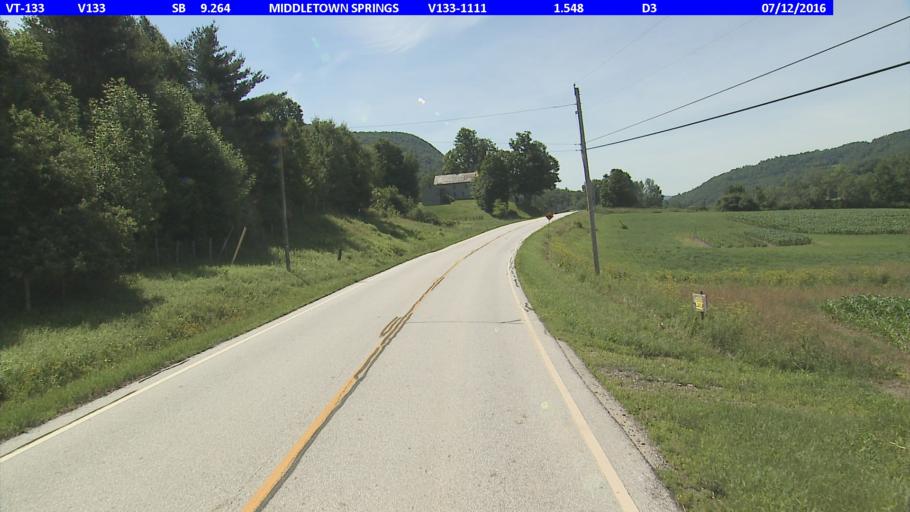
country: US
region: Vermont
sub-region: Rutland County
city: Poultney
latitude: 43.4575
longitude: -73.1098
